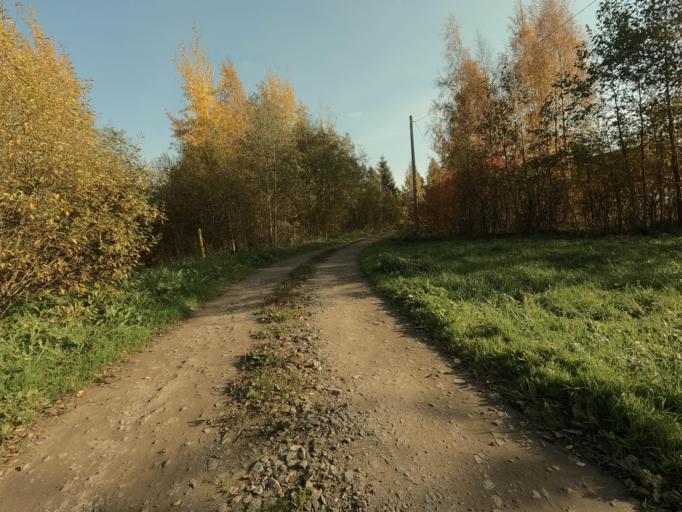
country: RU
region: Leningrad
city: Mga
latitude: 59.7482
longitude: 31.0695
